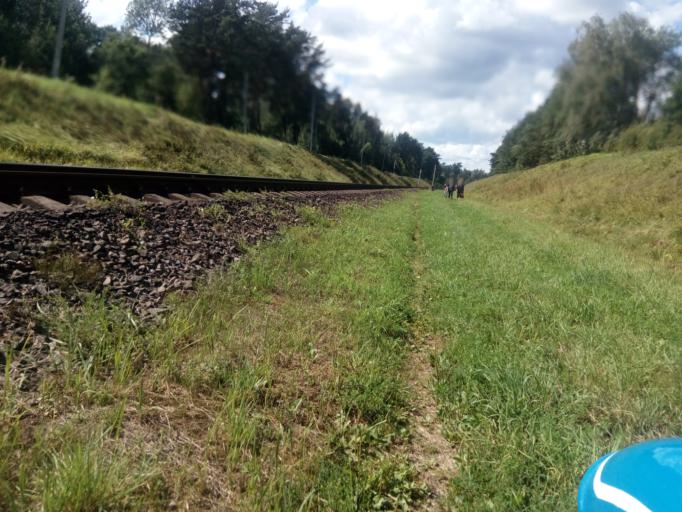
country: BY
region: Vitebsk
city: Dzisna
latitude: 55.6786
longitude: 28.2964
